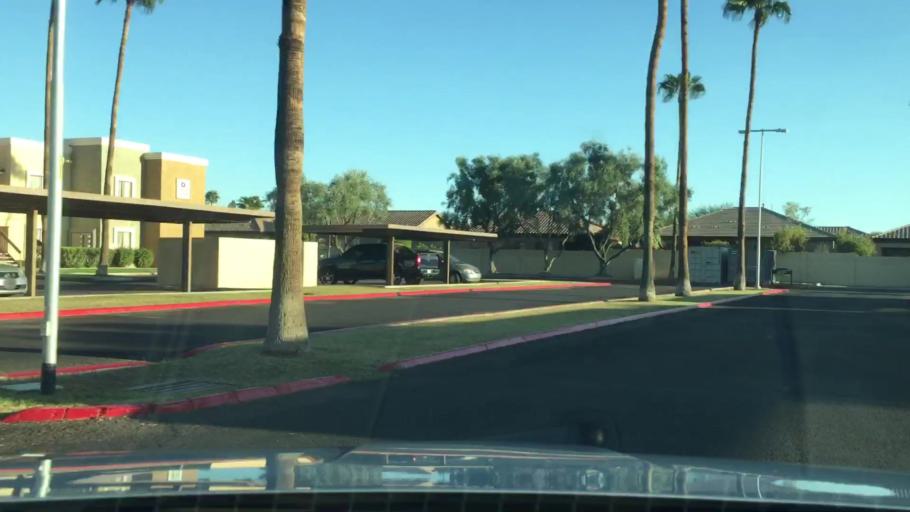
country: US
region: Arizona
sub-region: Maricopa County
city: Chandler
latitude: 33.3259
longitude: -111.8266
